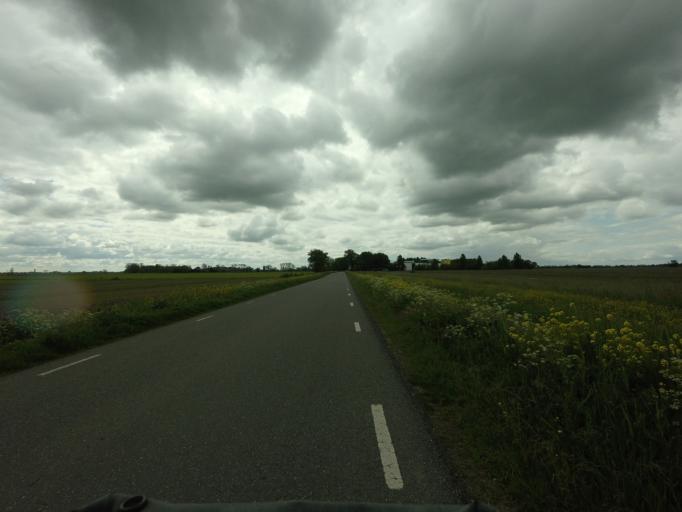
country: NL
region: Utrecht
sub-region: Gemeente Lopik
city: Lopik
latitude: 51.9387
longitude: 4.9357
